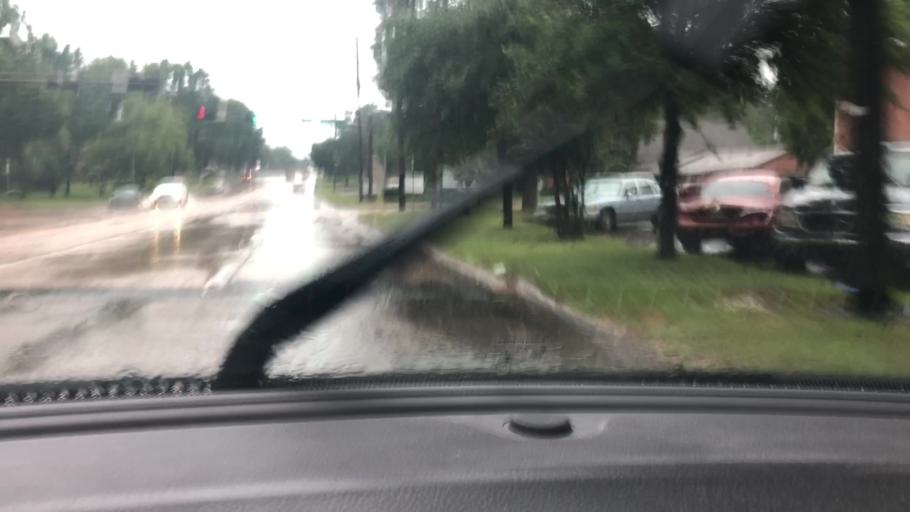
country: US
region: Texas
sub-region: Bowie County
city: Wake Village
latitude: 33.4467
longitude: -94.0805
